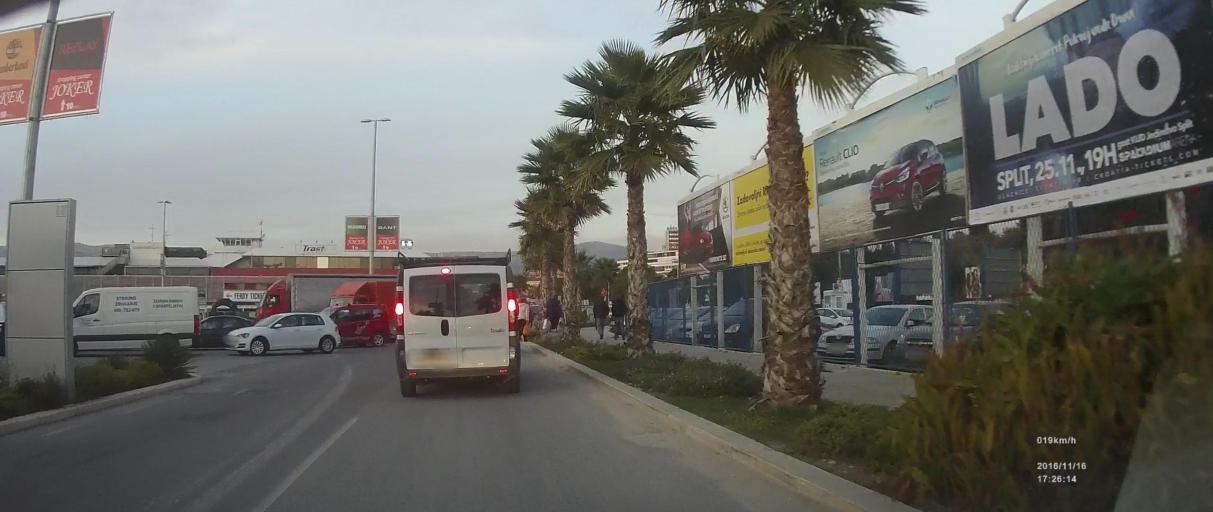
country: HR
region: Splitsko-Dalmatinska
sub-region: Grad Split
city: Split
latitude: 43.5019
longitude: 16.4423
